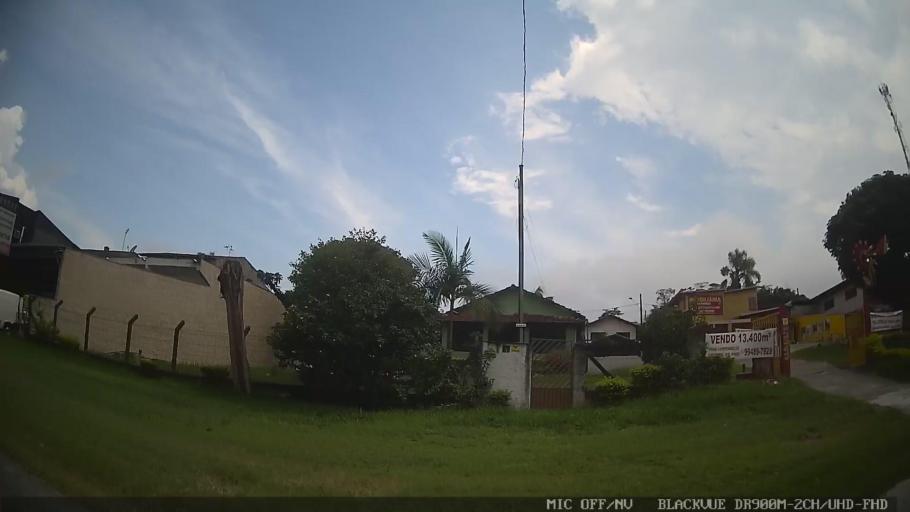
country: BR
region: Sao Paulo
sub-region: Ribeirao Pires
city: Ribeirao Pires
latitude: -23.6821
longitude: -46.3653
